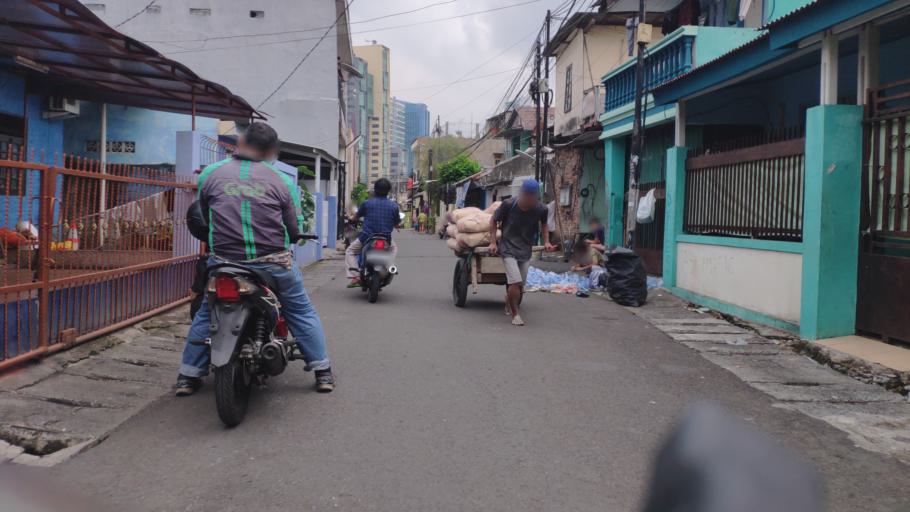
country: ID
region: Jakarta Raya
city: Jakarta
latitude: -6.2128
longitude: 106.8388
